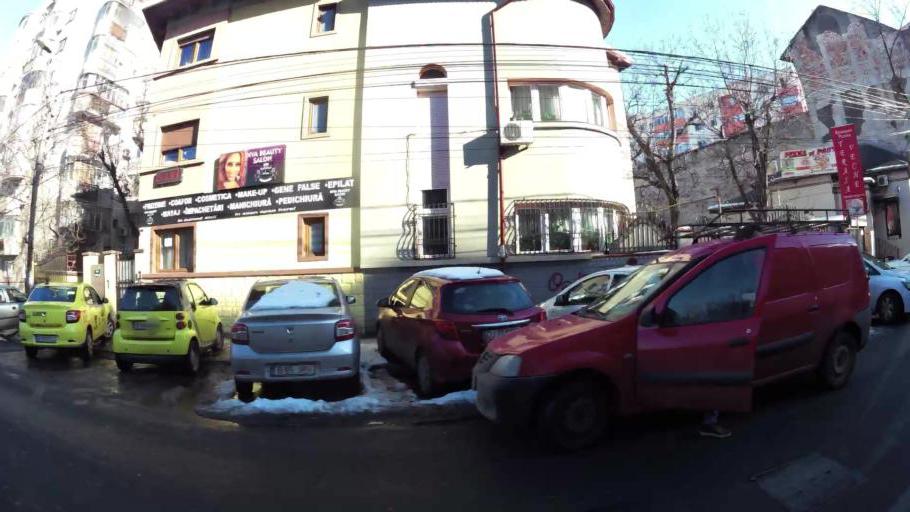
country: RO
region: Bucuresti
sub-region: Municipiul Bucuresti
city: Bucharest
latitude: 44.4615
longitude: 26.1267
